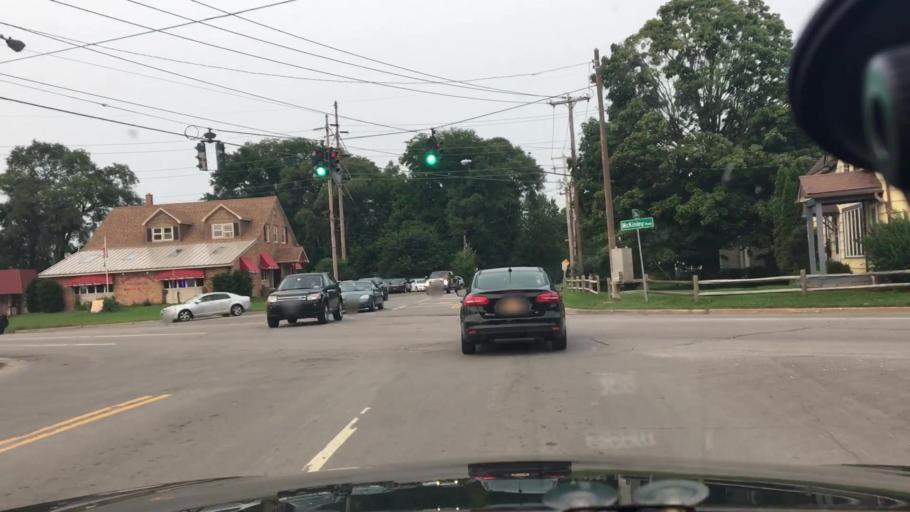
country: US
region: New York
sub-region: Erie County
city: Hamburg
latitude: 42.7319
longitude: -78.8130
